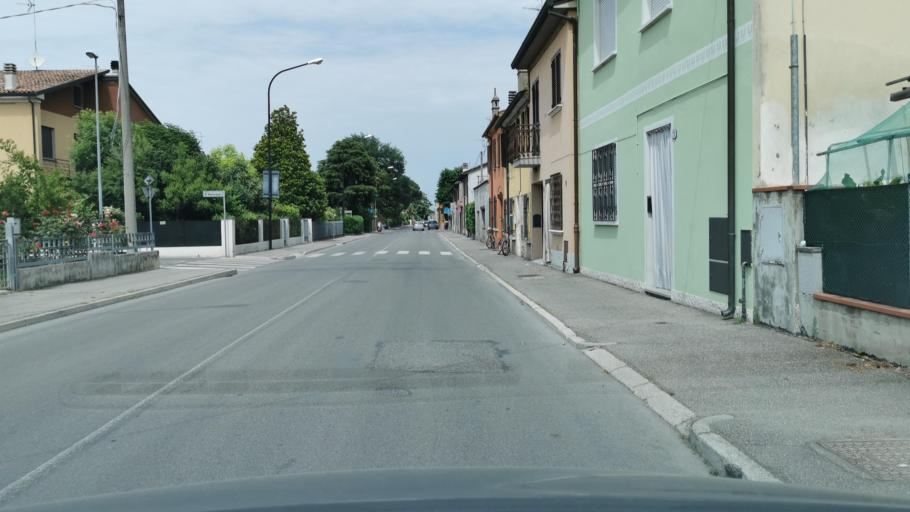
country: IT
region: Emilia-Romagna
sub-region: Provincia di Ravenna
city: Bagnacavallo
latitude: 44.4158
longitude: 11.9723
